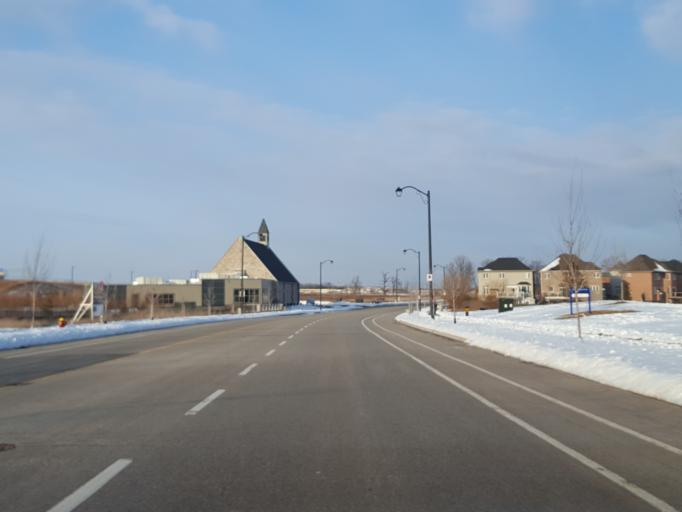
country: CA
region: Ontario
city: Burlington
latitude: 43.4081
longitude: -79.8252
